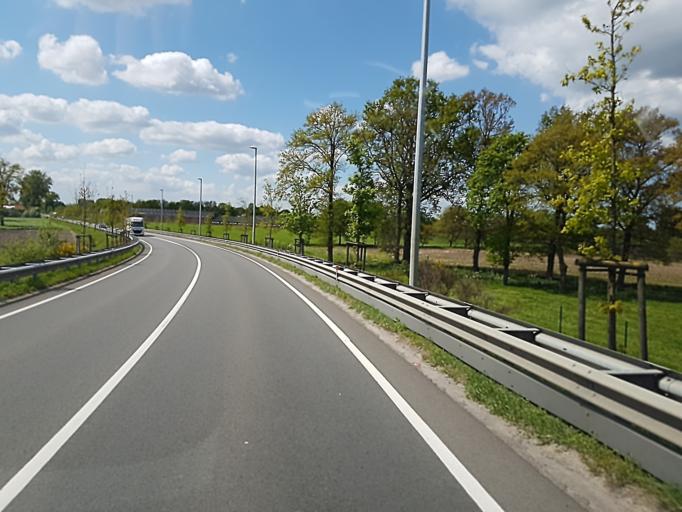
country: BE
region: Flanders
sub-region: Provincie Antwerpen
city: Brecht
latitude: 51.3602
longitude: 4.6319
